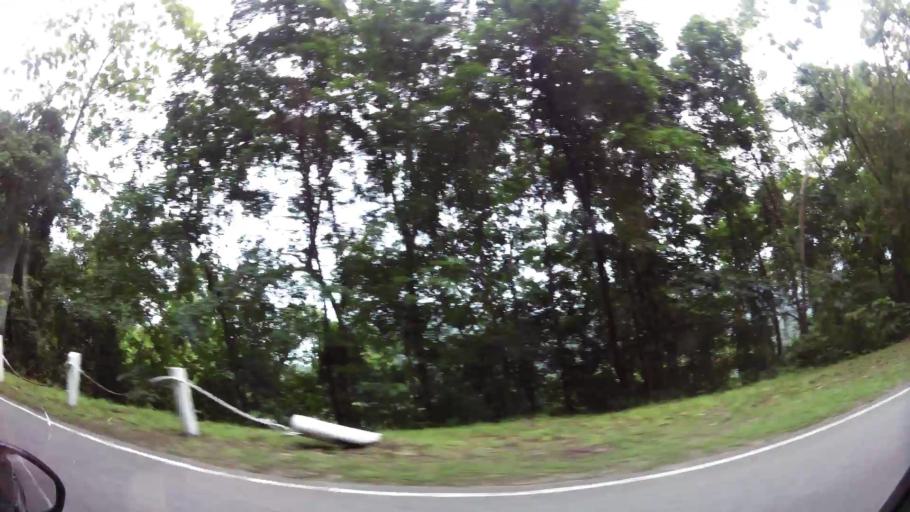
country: TT
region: Diego Martin
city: Petit Valley
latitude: 10.7381
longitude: -61.4932
